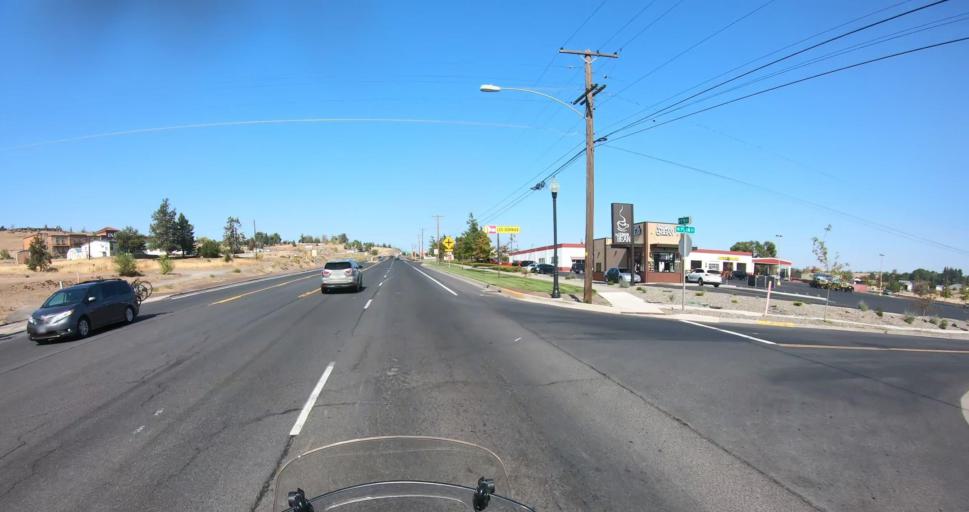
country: US
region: Oregon
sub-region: Jefferson County
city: Madras
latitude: 44.6415
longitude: -121.1311
